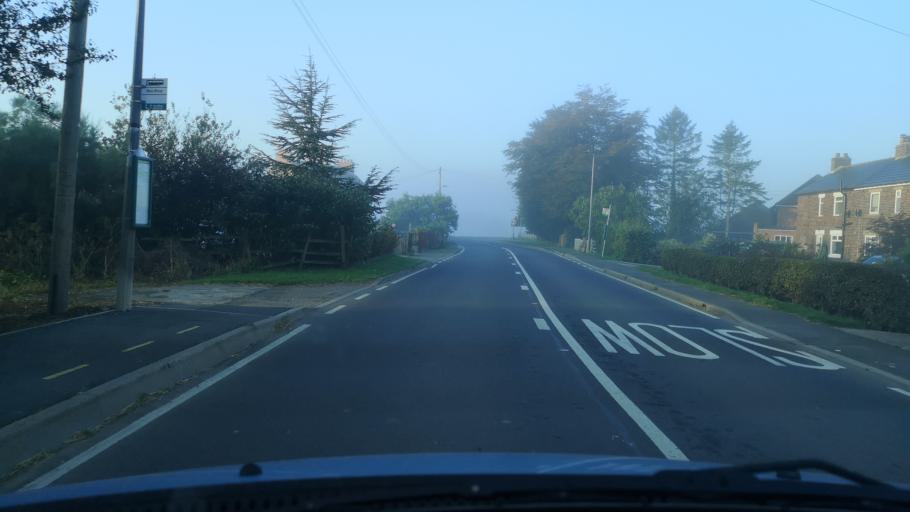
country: GB
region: England
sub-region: North Lincolnshire
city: Eastoft
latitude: 53.6339
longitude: -0.7895
